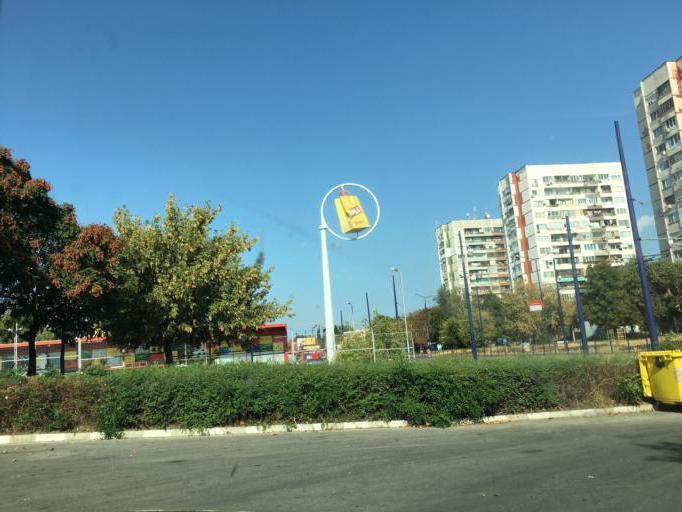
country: BG
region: Pazardzhik
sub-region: Obshtina Pazardzhik
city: Pazardzhik
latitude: 42.1861
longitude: 24.3218
